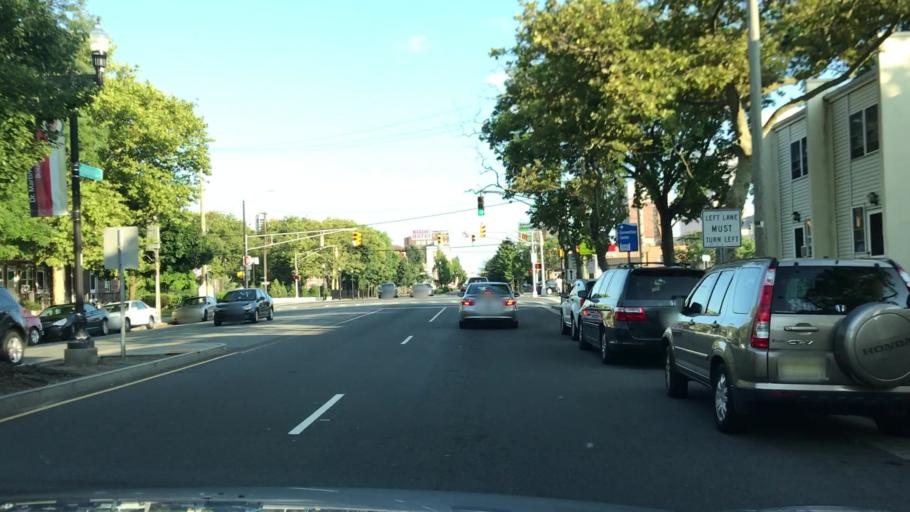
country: US
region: New Jersey
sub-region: Atlantic County
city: Atlantic City
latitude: 39.3641
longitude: -74.4343
